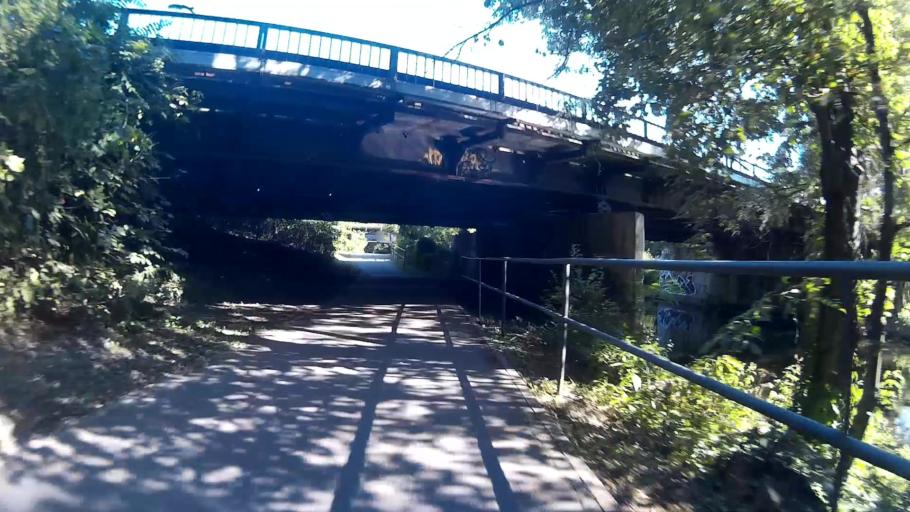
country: CZ
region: South Moravian
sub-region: Mesto Brno
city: Brno
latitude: 49.1795
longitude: 16.6131
